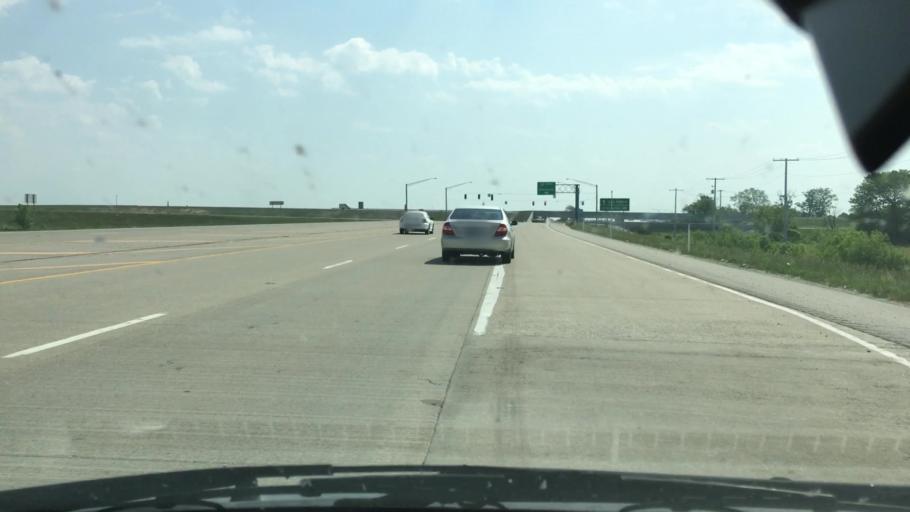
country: US
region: Indiana
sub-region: Daviess County
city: Washington
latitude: 38.6551
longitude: -87.1260
